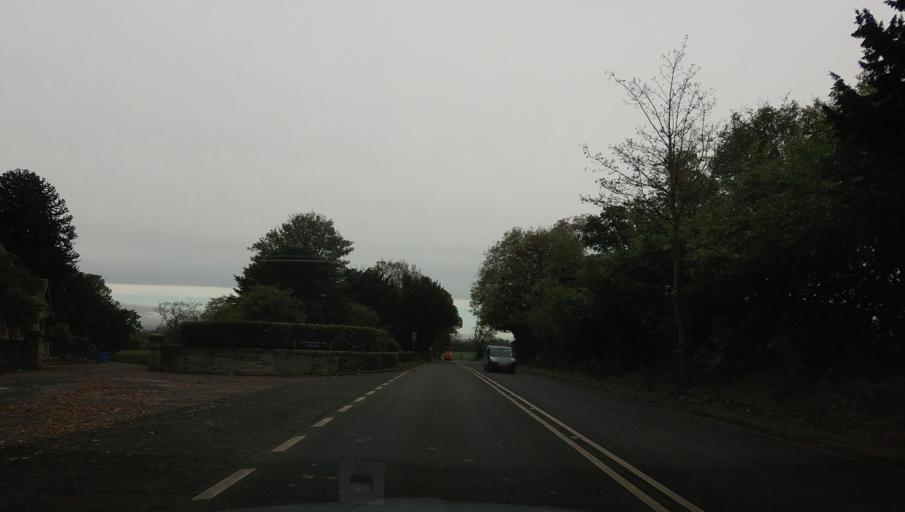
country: GB
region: Scotland
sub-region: Fife
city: Limekilns
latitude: 56.0402
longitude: -3.4710
